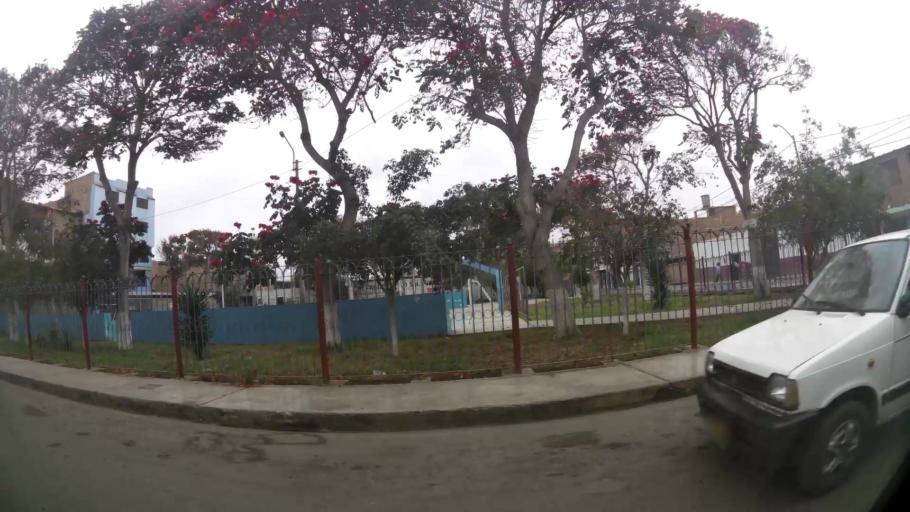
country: PE
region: La Libertad
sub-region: Provincia de Trujillo
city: Trujillo
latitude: -8.1054
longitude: -79.0419
